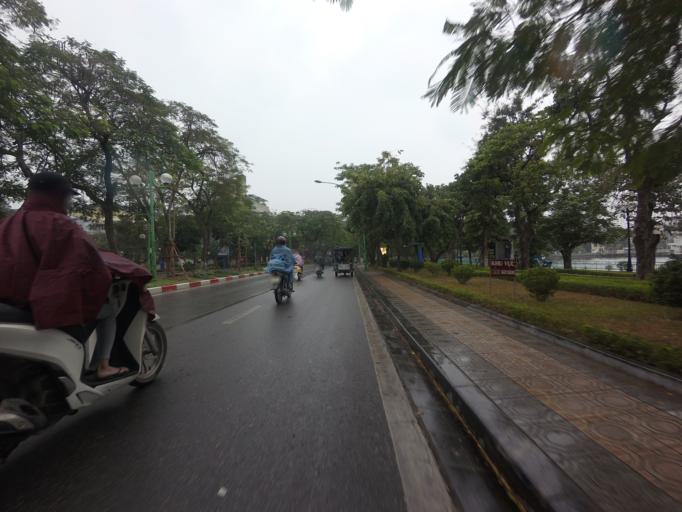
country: VN
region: Ha Noi
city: Hanoi
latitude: 21.0448
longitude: 105.8362
